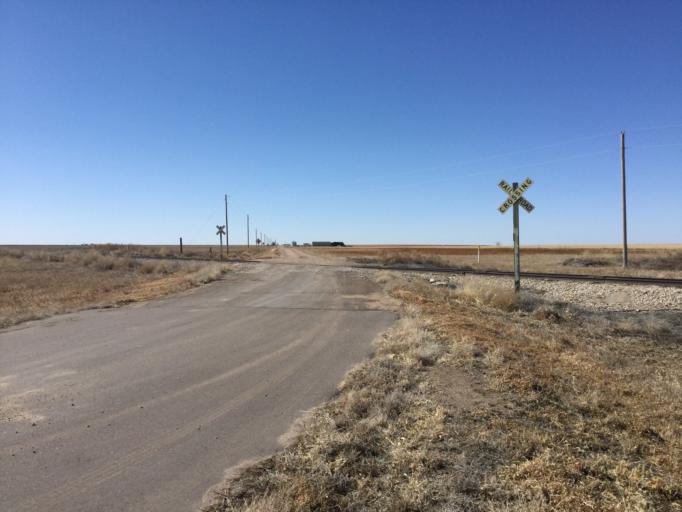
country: US
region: Kansas
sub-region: Sheridan County
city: Hoxie
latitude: 39.5098
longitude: -100.6475
